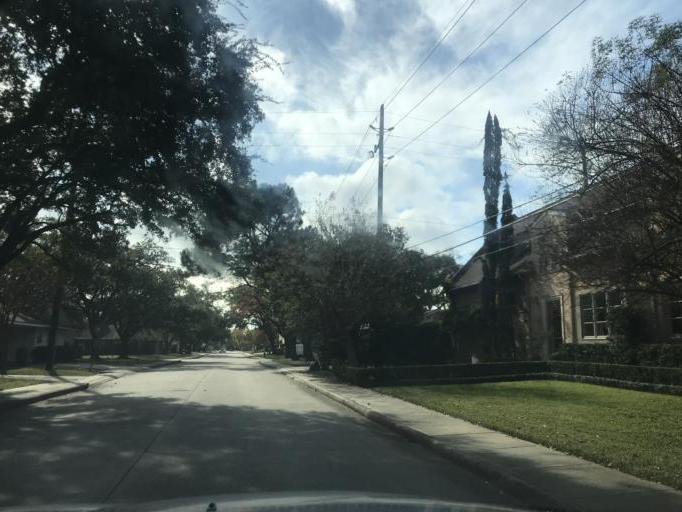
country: US
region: Texas
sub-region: Harris County
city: Hunters Creek Village
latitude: 29.7449
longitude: -95.4925
